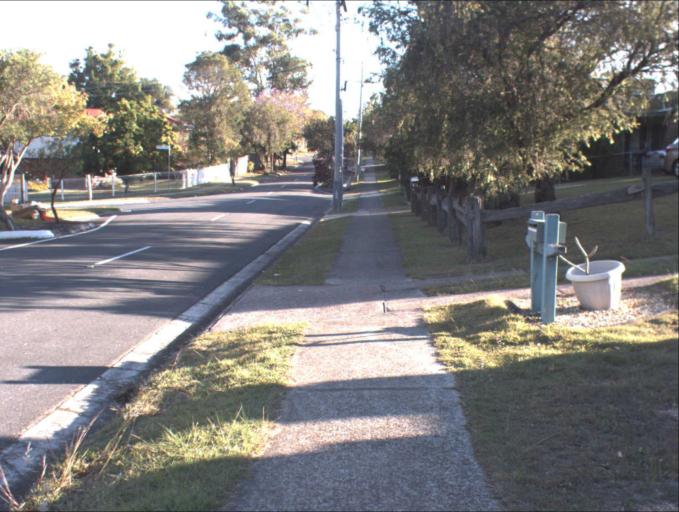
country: AU
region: Queensland
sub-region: Logan
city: Slacks Creek
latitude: -27.6473
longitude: 153.1295
